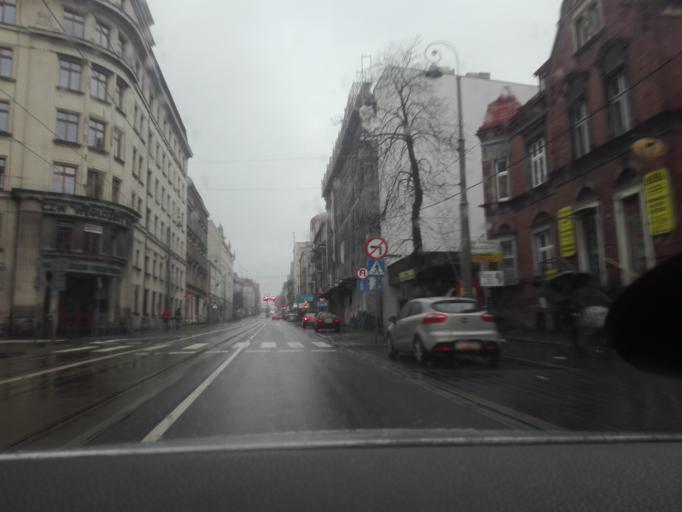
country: PL
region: Silesian Voivodeship
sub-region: Katowice
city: Katowice
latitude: 50.2538
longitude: 19.0169
